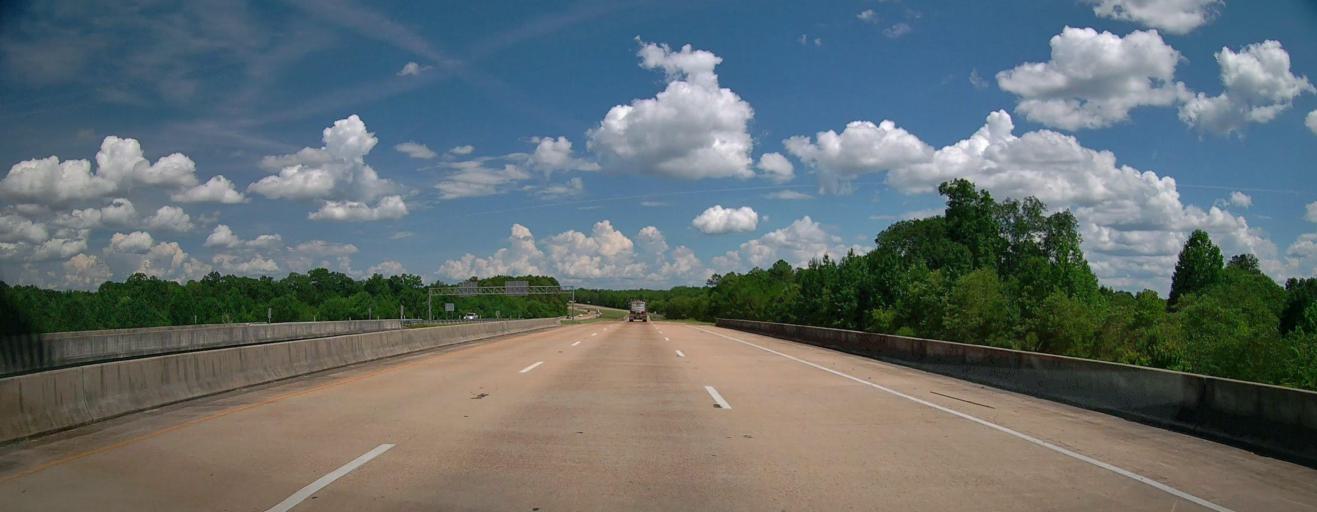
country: US
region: Mississippi
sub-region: Monroe County
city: Aberdeen
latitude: 33.8127
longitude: -88.4901
